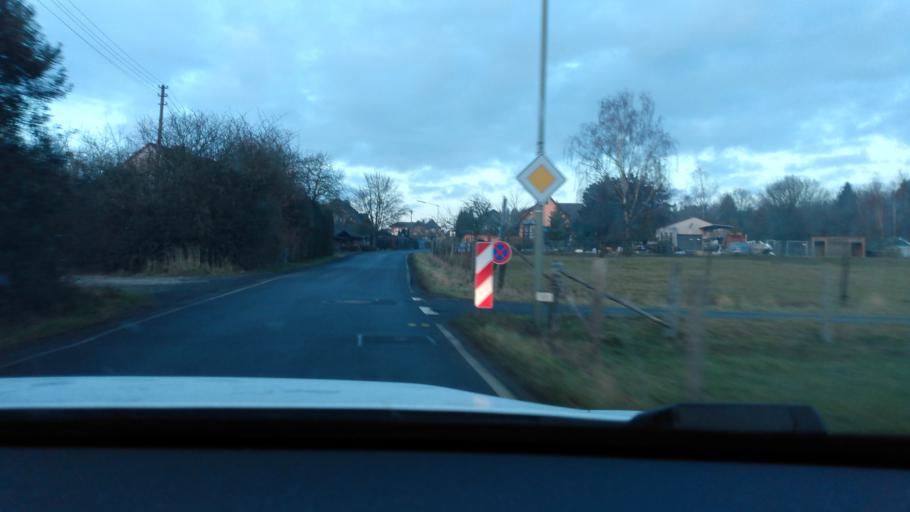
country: DE
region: Rheinland-Pfalz
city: Kircheib
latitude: 50.7048
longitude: 7.4678
